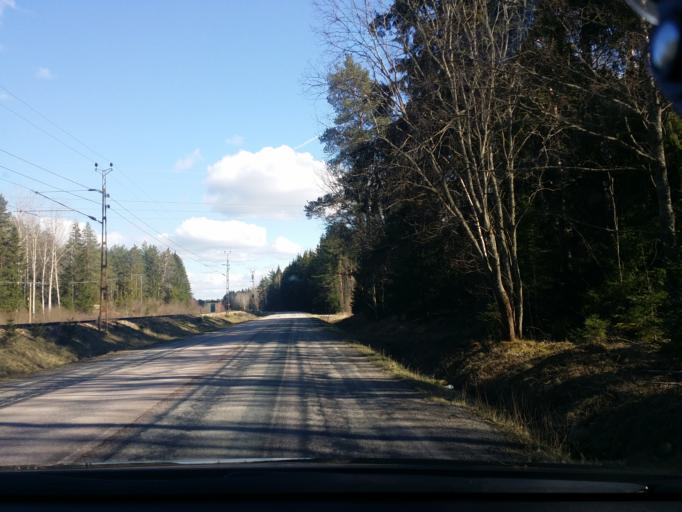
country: SE
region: Vaestmanland
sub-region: Sala Kommun
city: Sala
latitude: 59.9518
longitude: 16.5258
